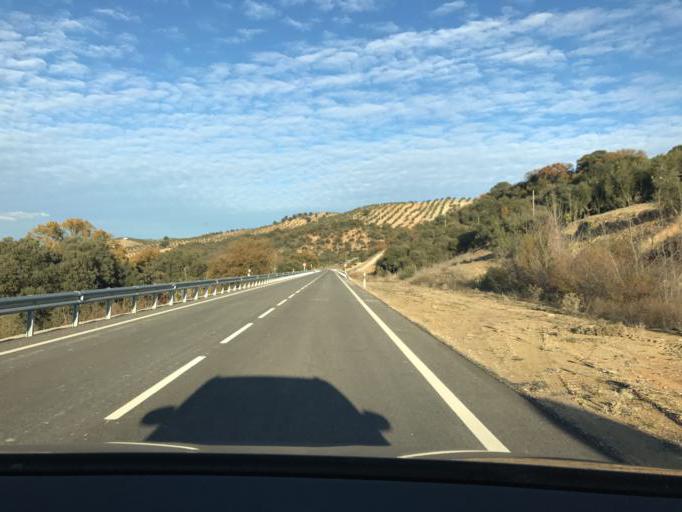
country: ES
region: Andalusia
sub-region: Provincia de Granada
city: Pinar
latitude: 37.4308
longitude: -3.4796
